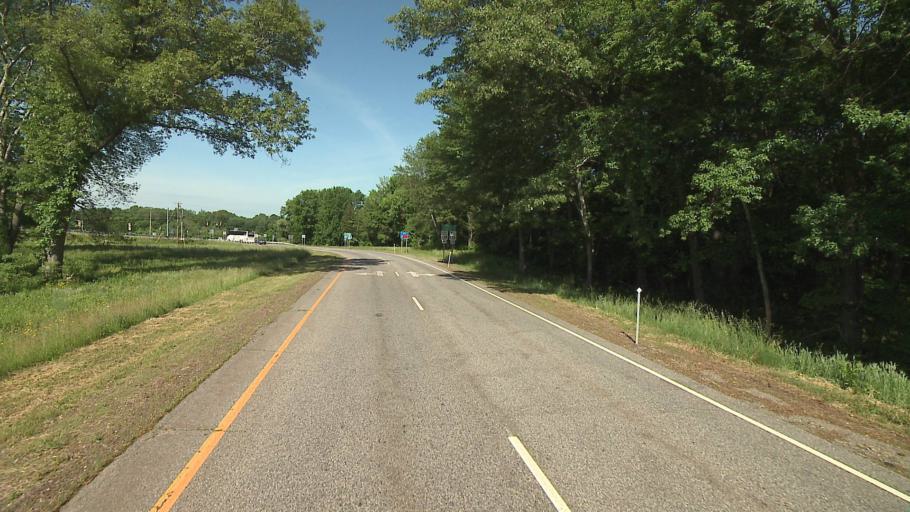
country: US
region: Connecticut
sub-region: New London County
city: Jewett City
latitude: 41.5943
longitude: -71.9705
